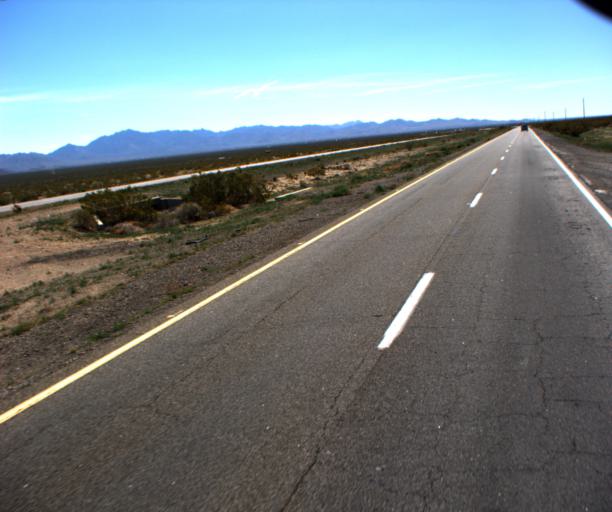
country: US
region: Arizona
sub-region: Mohave County
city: Dolan Springs
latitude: 35.6173
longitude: -114.4171
